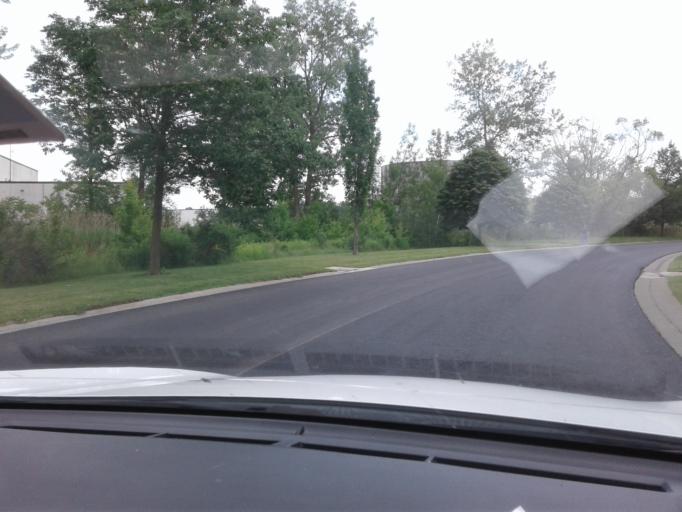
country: US
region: New York
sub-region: Onondaga County
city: East Syracuse
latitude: 43.0886
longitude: -76.0758
